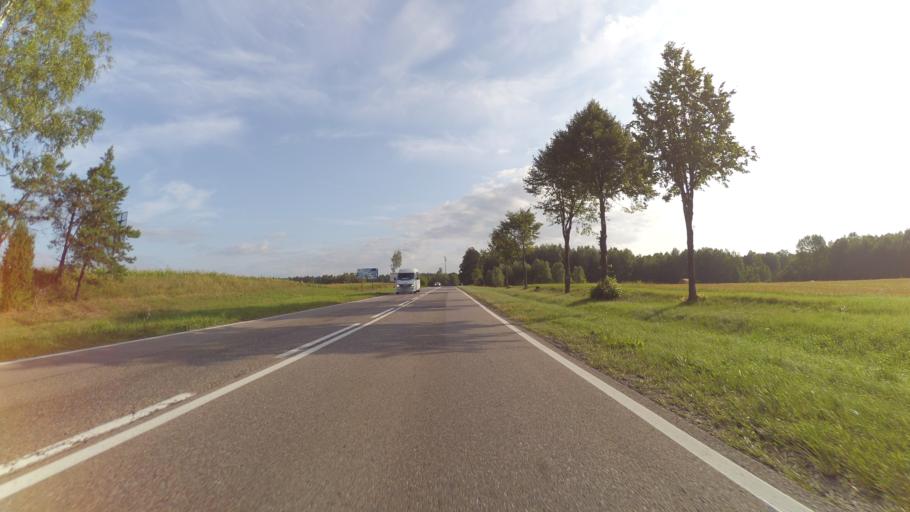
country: PL
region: Podlasie
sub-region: Powiat bialostocki
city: Wasilkow
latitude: 53.2497
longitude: 23.2423
